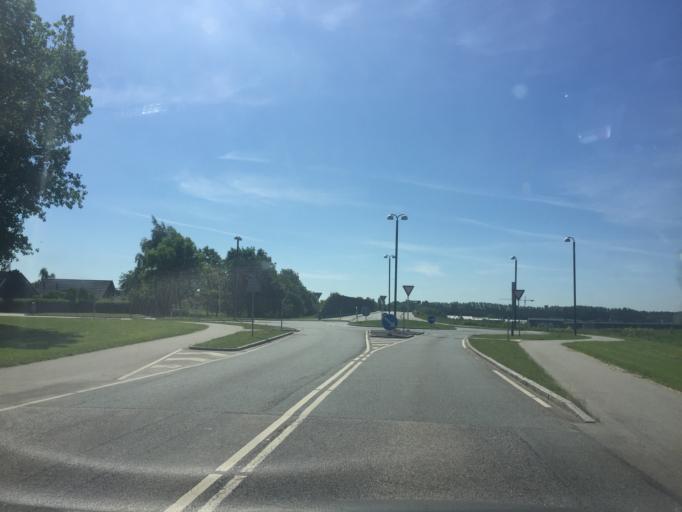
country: DK
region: Capital Region
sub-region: Hoje-Taastrup Kommune
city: Flong
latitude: 55.6577
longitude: 12.1763
